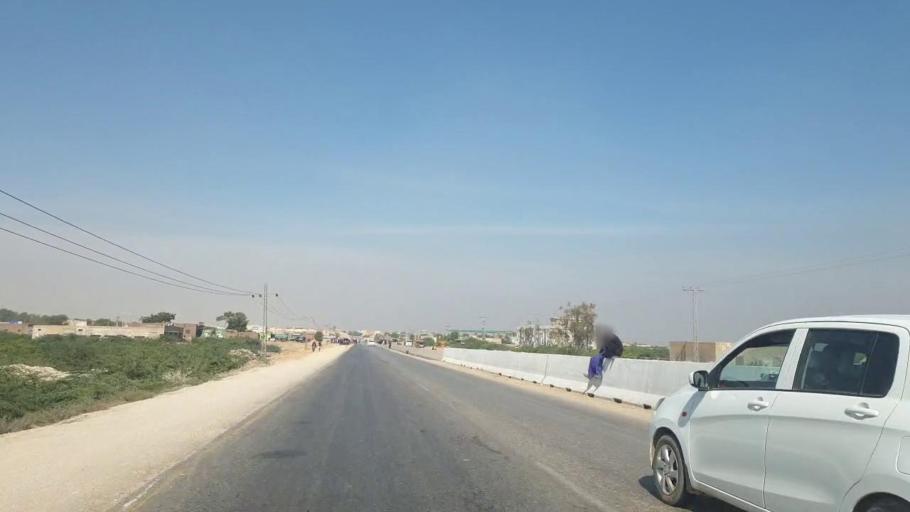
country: PK
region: Sindh
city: Hala
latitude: 25.7243
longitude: 68.2929
